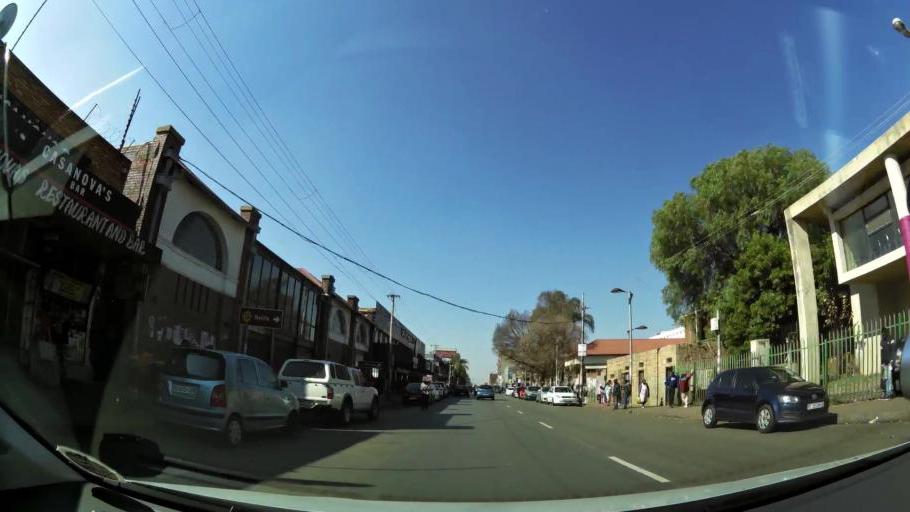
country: ZA
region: Gauteng
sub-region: City of Johannesburg Metropolitan Municipality
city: Johannesburg
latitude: -26.1813
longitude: 28.0621
